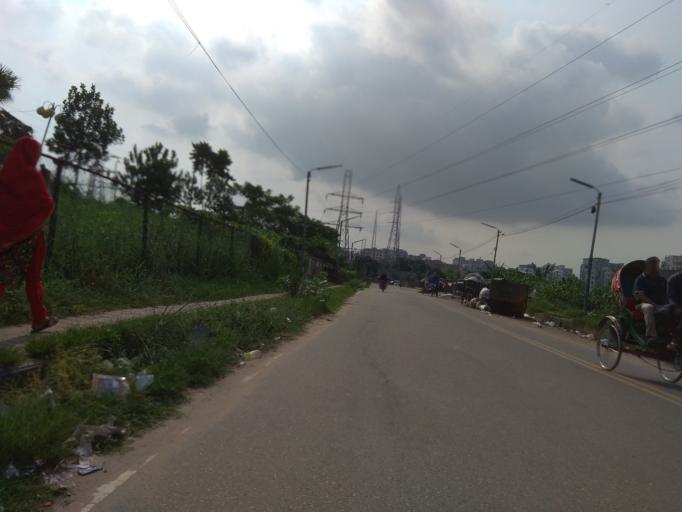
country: BD
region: Dhaka
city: Tungi
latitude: 23.8303
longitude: 90.3574
